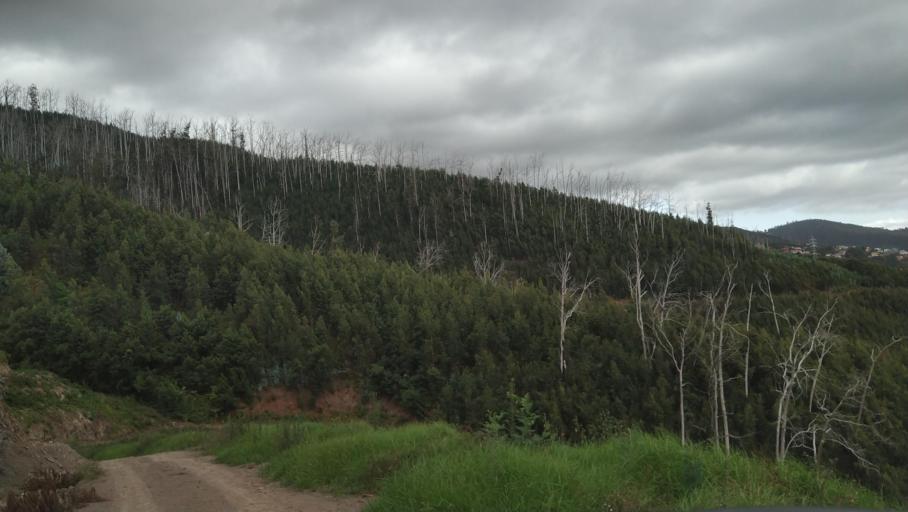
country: PT
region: Madeira
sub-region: Funchal
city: Nossa Senhora do Monte
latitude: 32.6804
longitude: -16.9278
